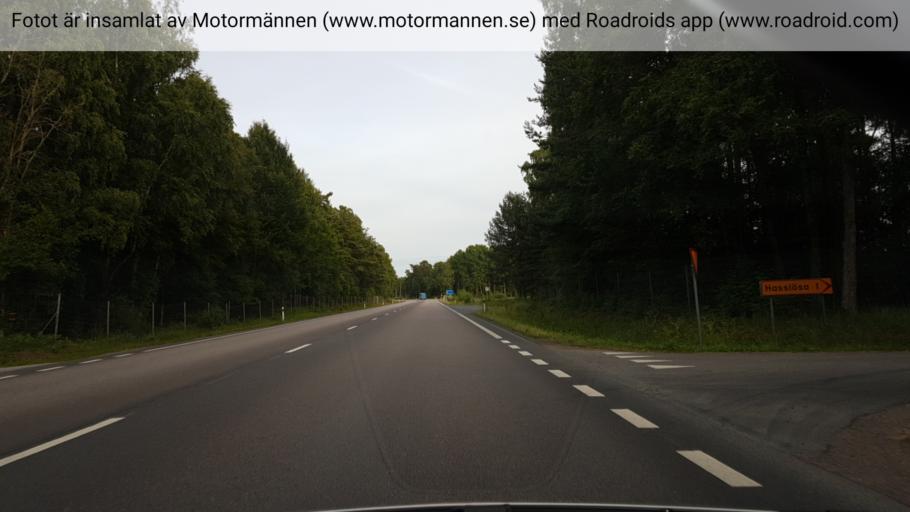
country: SE
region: Vaestra Goetaland
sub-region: Lidkopings Kommun
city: Vinninga
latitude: 58.4348
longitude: 13.2829
